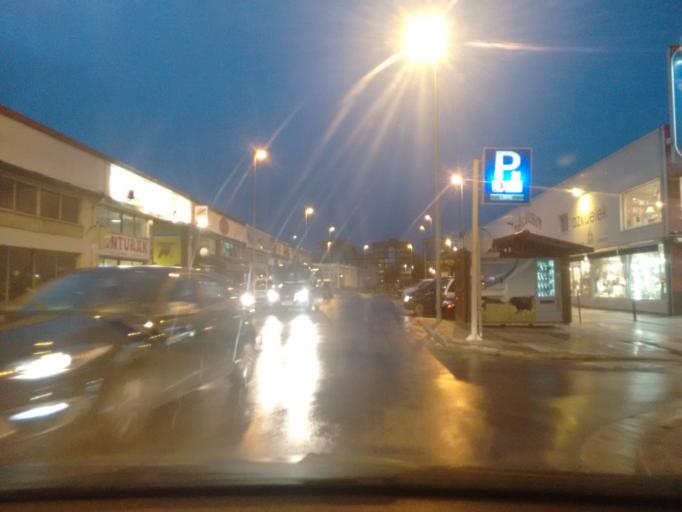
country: ES
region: Basque Country
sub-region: Provincia de Guipuzcoa
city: Zarautz
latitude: 43.2812
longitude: -2.1654
